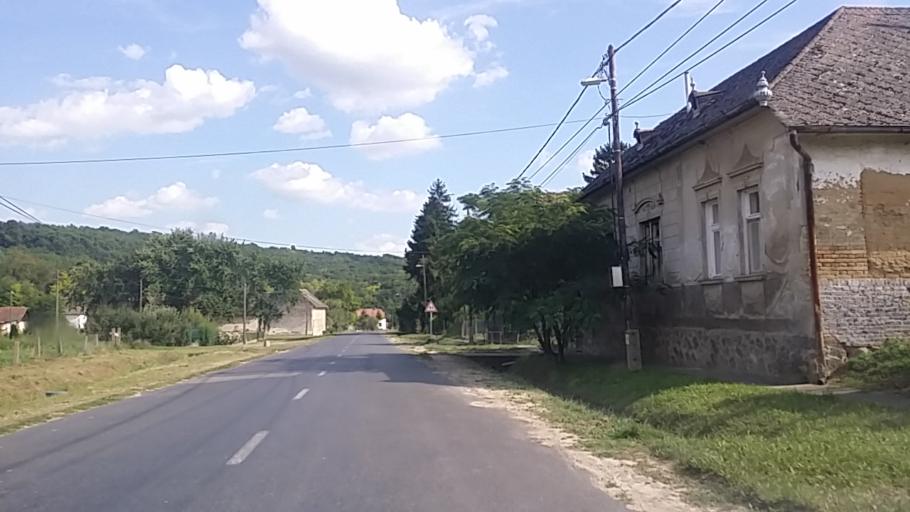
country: HU
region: Tolna
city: Zomba
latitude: 46.5033
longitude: 18.5627
